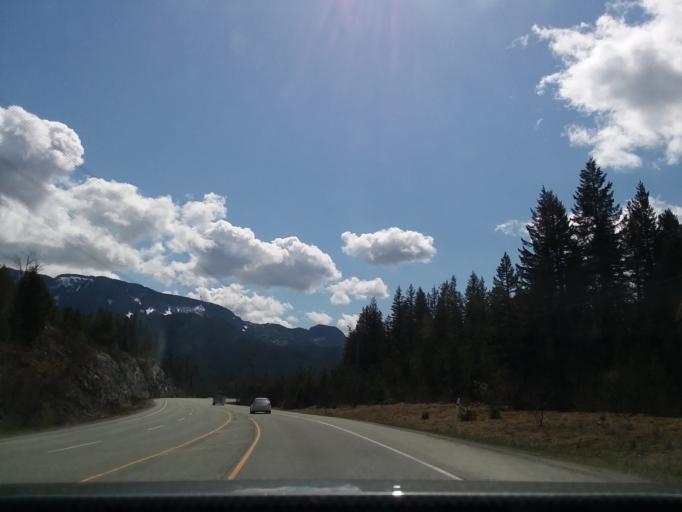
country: CA
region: British Columbia
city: Whistler
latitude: 49.9840
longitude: -123.1435
